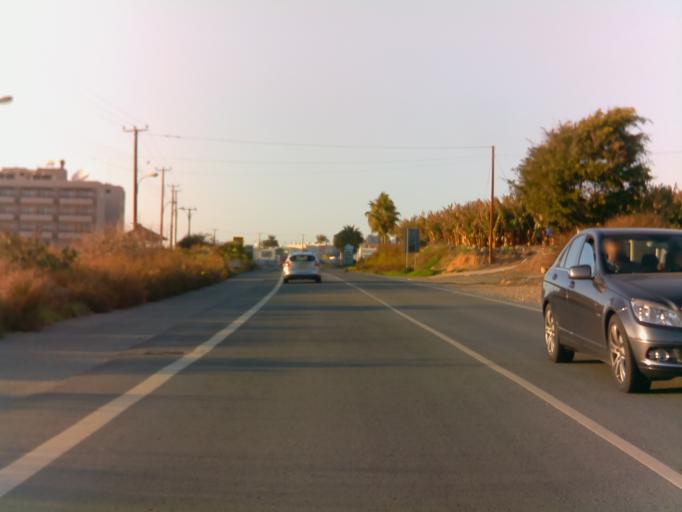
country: CY
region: Pafos
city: Kissonerga
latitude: 34.8199
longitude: 32.3948
